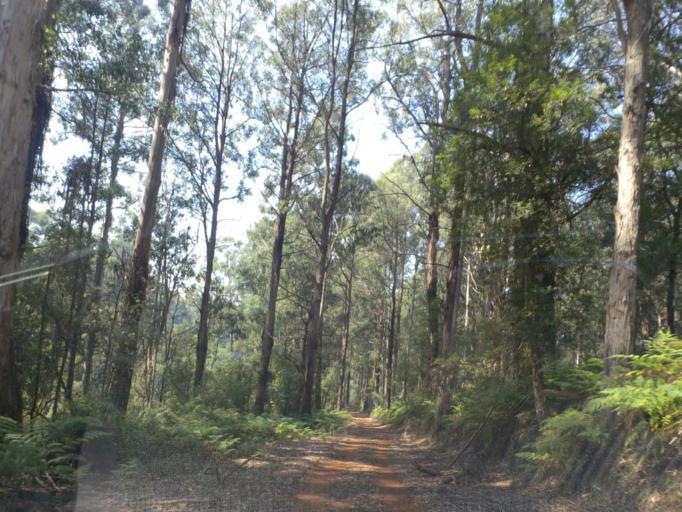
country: AU
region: Victoria
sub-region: Yarra Ranges
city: Healesville
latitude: -37.5596
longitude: 145.6261
